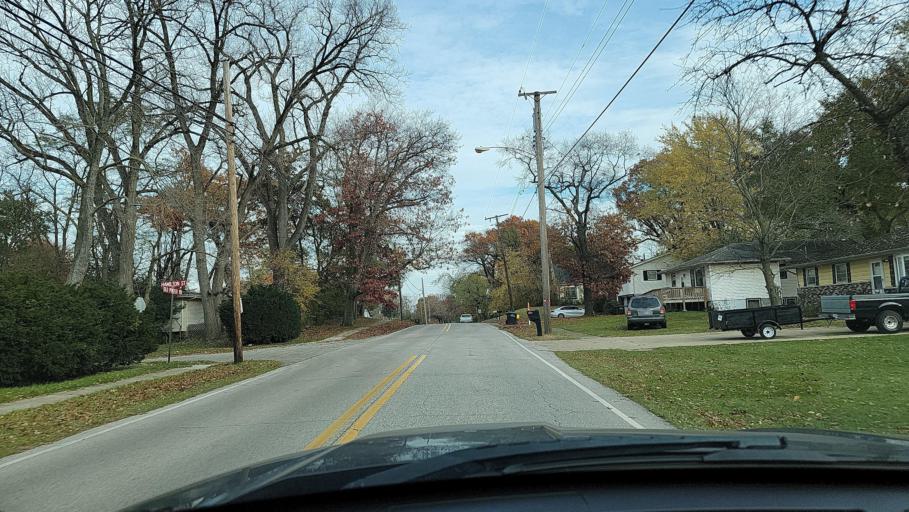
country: US
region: Indiana
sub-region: Porter County
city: Portage
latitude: 41.5941
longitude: -87.1582
